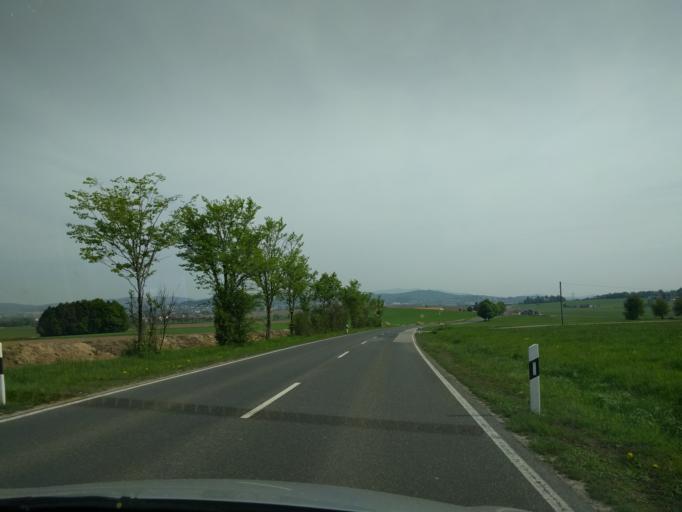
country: DE
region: Bavaria
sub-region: Upper Palatinate
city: Traitsching
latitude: 49.1864
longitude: 12.6366
